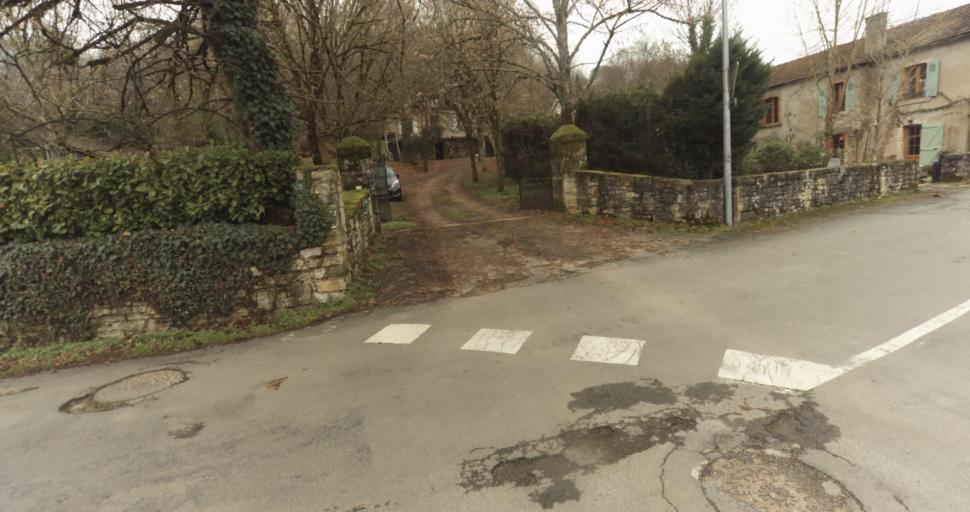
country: FR
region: Midi-Pyrenees
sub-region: Departement du Lot
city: Figeac
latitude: 44.6057
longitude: 2.0394
